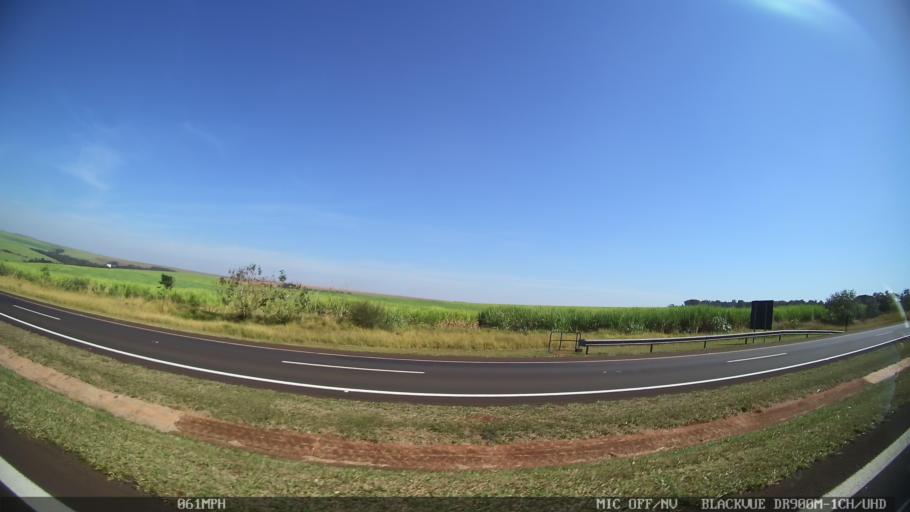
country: BR
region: Sao Paulo
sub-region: Ribeirao Preto
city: Ribeirao Preto
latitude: -21.1857
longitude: -47.8892
